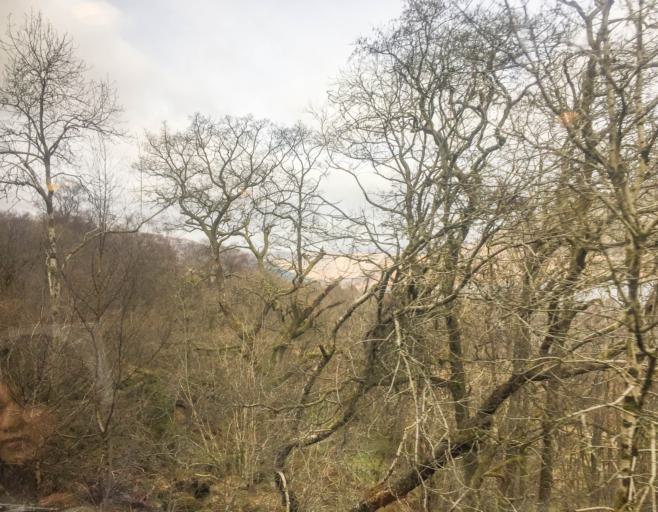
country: GB
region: Scotland
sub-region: Argyll and Bute
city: Garelochhead
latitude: 56.2857
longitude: -4.7091
